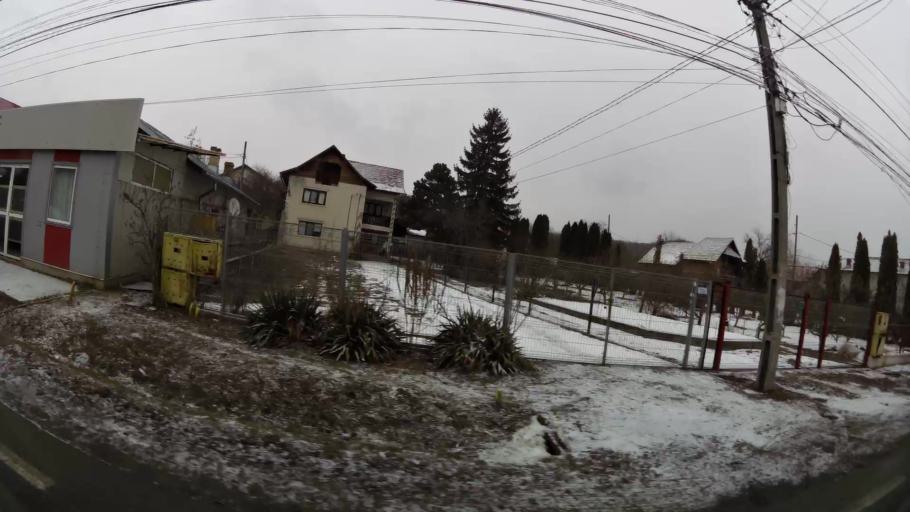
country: RO
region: Dambovita
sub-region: Comuna Aninoasa
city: Viforata
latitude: 44.9452
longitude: 25.4846
